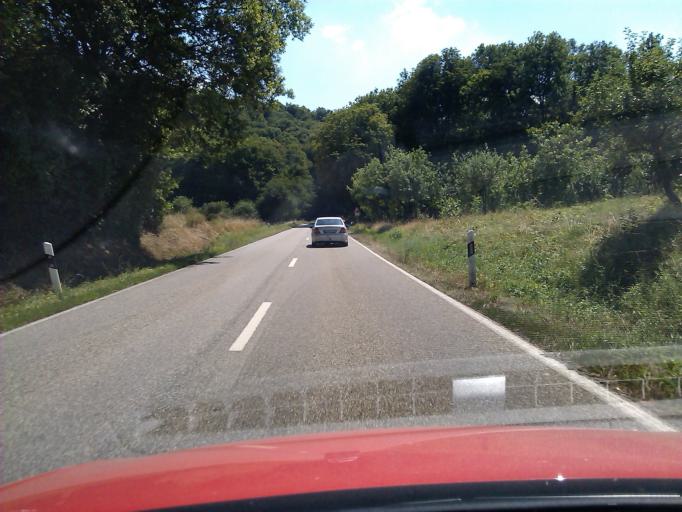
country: DE
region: Baden-Wuerttemberg
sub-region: Regierungsbezirk Stuttgart
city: Schwaigern
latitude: 49.1262
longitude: 9.0683
